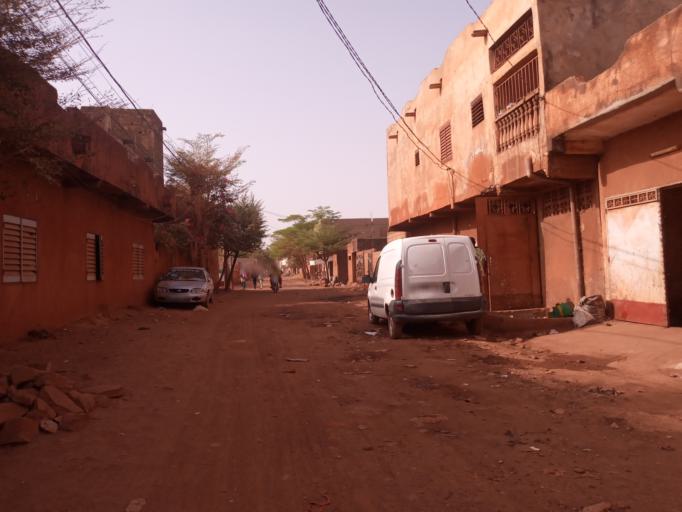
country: ML
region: Bamako
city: Bamako
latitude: 12.6811
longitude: -7.9406
